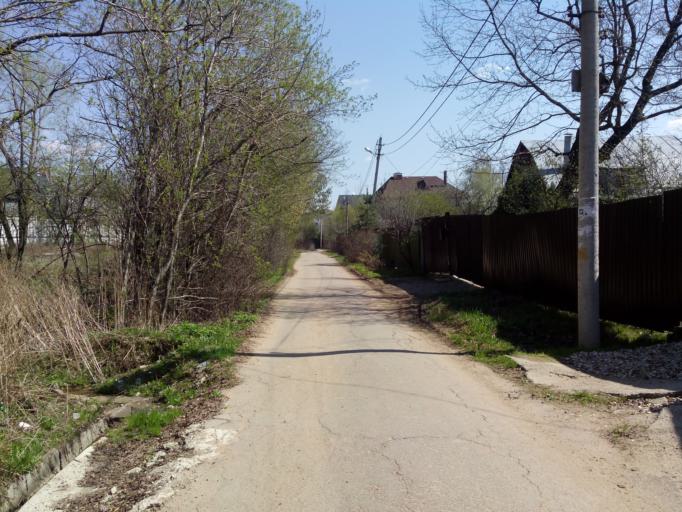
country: RU
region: Moskovskaya
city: Lesnoy Gorodok
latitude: 55.6629
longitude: 37.2338
